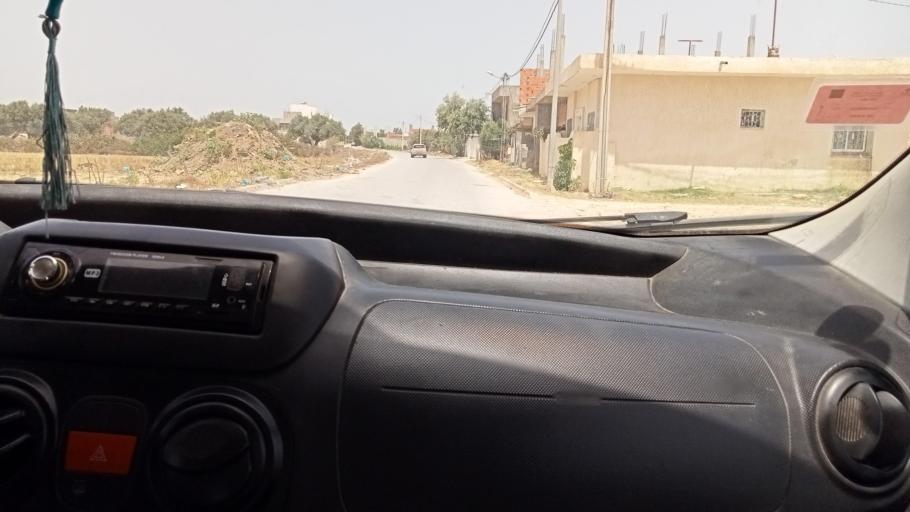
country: TN
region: Nabul
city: Qulaybiyah
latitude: 36.8613
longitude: 11.0871
